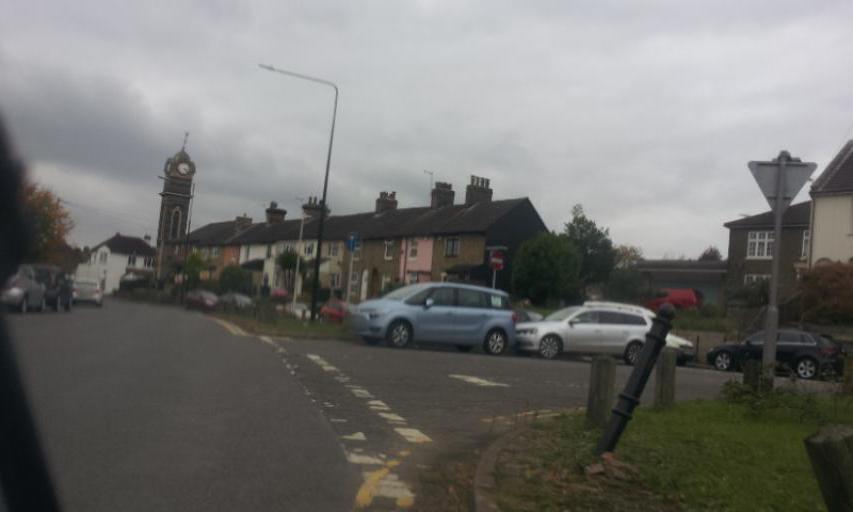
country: GB
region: England
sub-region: Kent
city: Snodland
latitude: 51.3343
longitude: 0.4451
